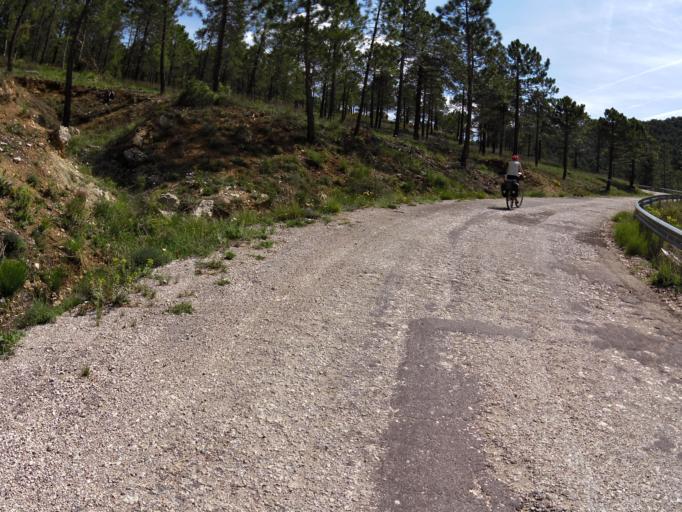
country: ES
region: Castille-La Mancha
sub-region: Provincia de Albacete
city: Riopar
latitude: 38.5256
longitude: -2.4307
